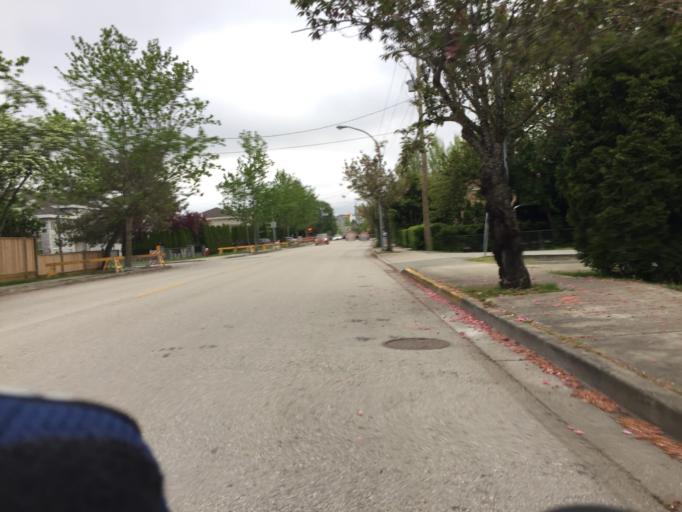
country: CA
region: British Columbia
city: Richmond
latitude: 49.1541
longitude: -123.1309
